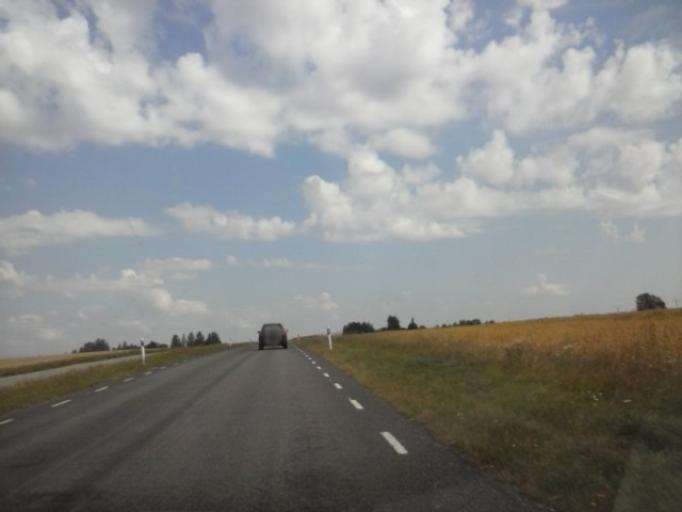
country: EE
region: Jogevamaa
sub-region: Tabivere vald
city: Tabivere
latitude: 58.5110
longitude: 26.6834
